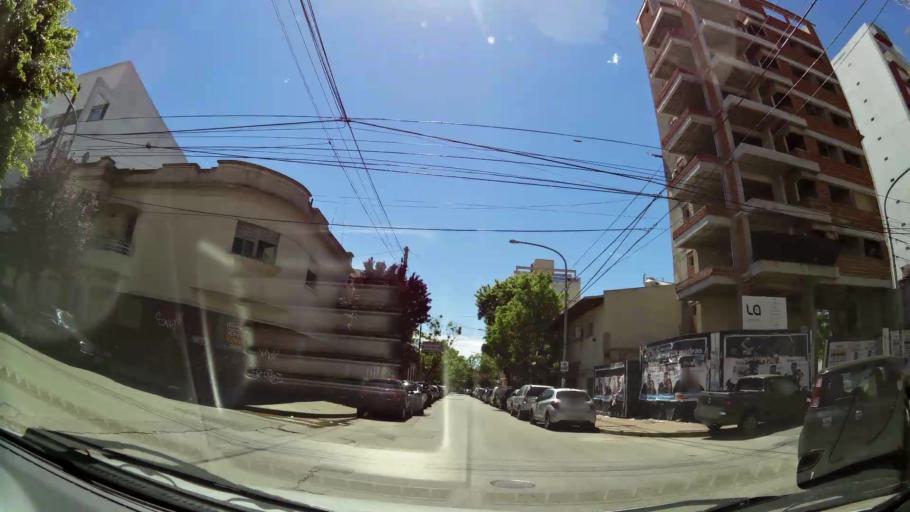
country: AR
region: Buenos Aires
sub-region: Partido de Quilmes
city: Quilmes
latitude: -34.7217
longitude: -58.2524
